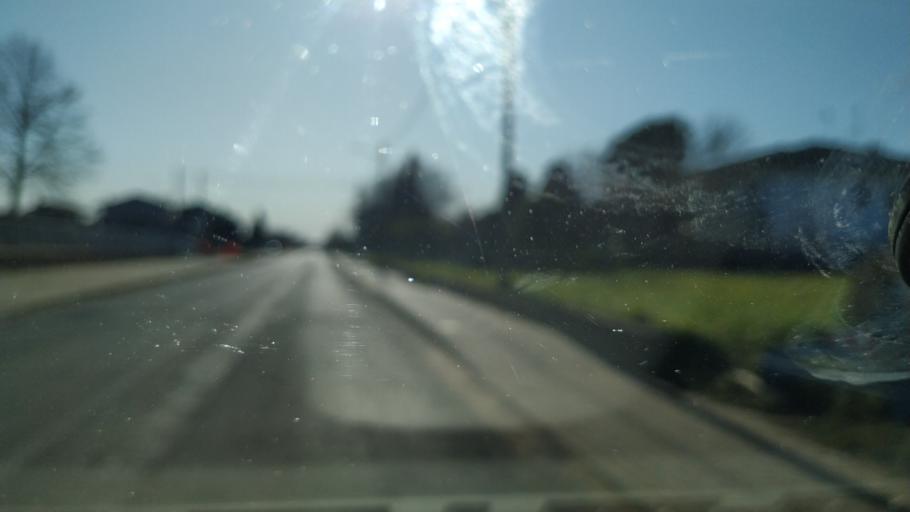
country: IT
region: Piedmont
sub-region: Provincia di Vercelli
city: Lozzolo
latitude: 45.6176
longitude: 8.3228
